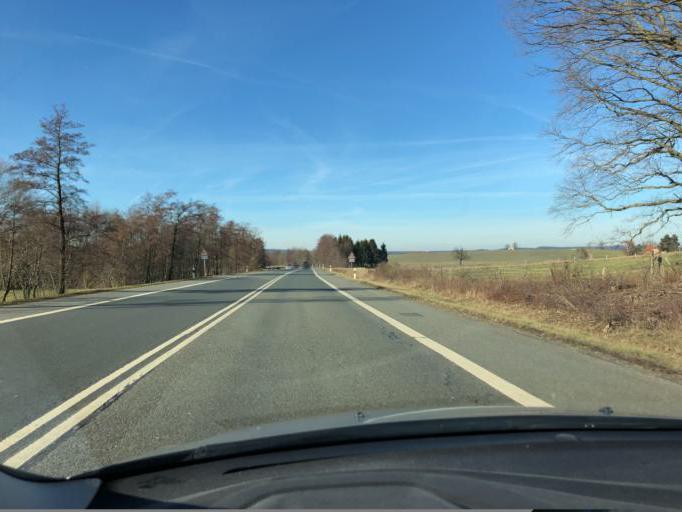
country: DE
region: Lower Saxony
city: Lutter am Barenberge
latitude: 51.9506
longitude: 10.2884
